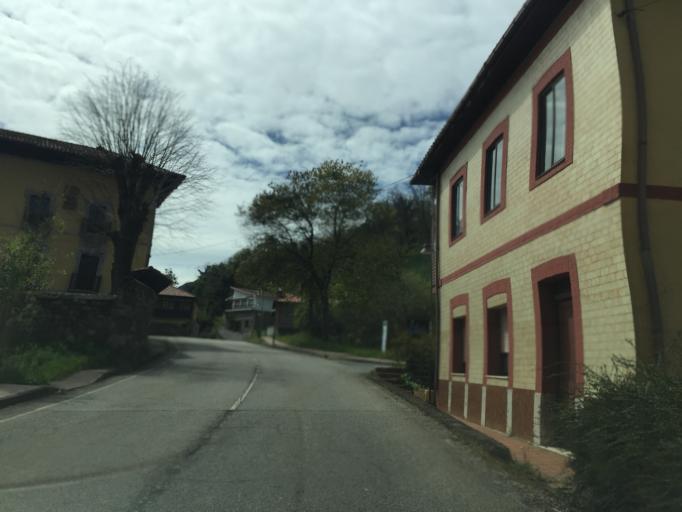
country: ES
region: Asturias
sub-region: Province of Asturias
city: Proaza
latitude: 43.2562
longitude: -6.0128
